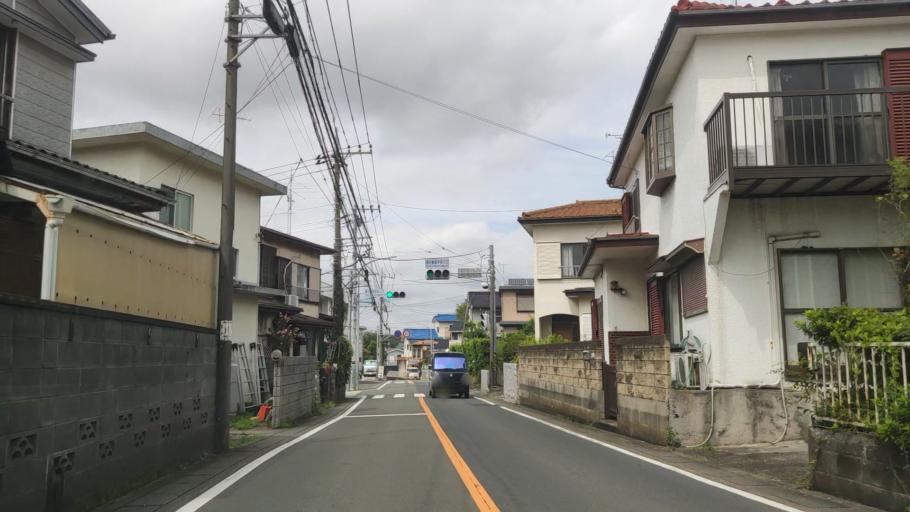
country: JP
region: Kanagawa
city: Minami-rinkan
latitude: 35.4855
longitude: 139.4740
